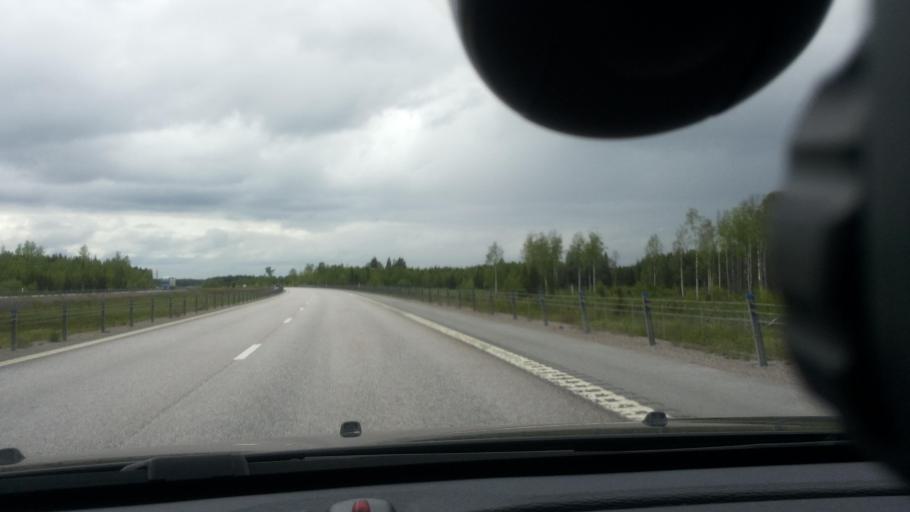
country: SE
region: Uppsala
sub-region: Tierps Kommun
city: Tierp
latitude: 60.4080
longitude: 17.4681
